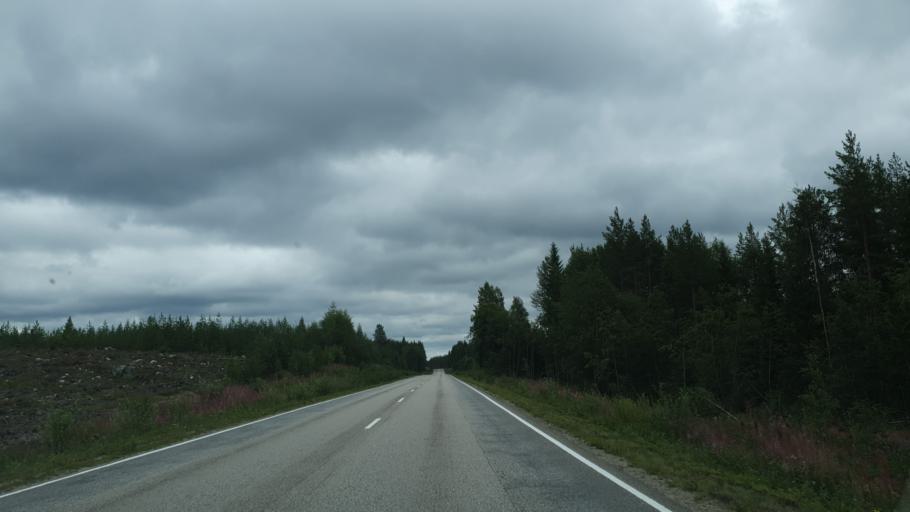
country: FI
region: Kainuu
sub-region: Kehys-Kainuu
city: Kuhmo
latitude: 64.1574
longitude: 29.3613
